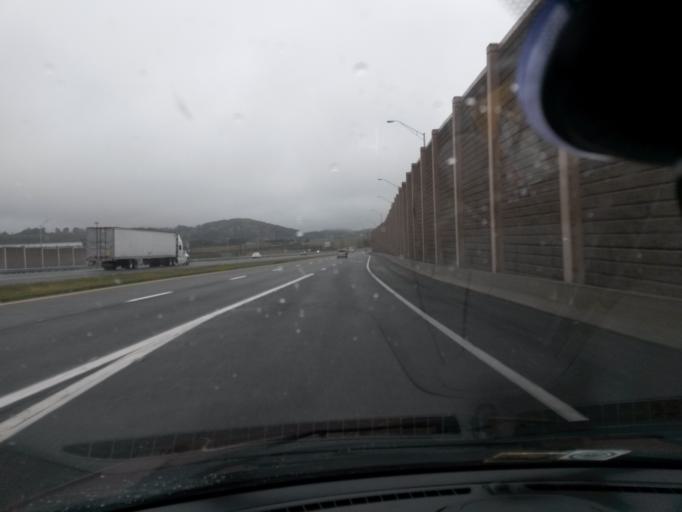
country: US
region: Virginia
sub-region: Montgomery County
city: Christiansburg
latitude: 37.1279
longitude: -80.3747
